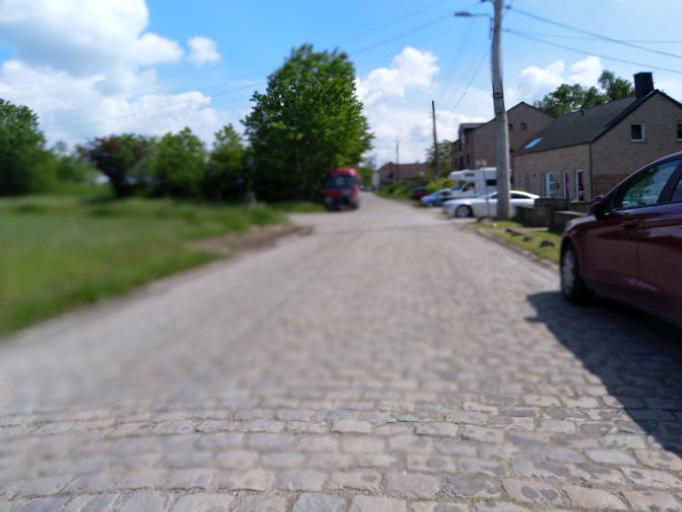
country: BE
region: Wallonia
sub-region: Province du Hainaut
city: Mons
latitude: 50.4935
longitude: 4.0060
